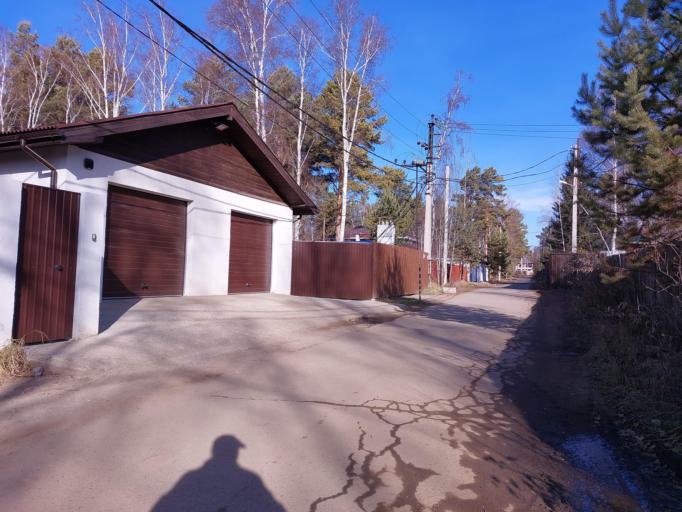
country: RU
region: Irkutsk
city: Pivovarikha
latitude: 52.1876
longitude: 104.4544
